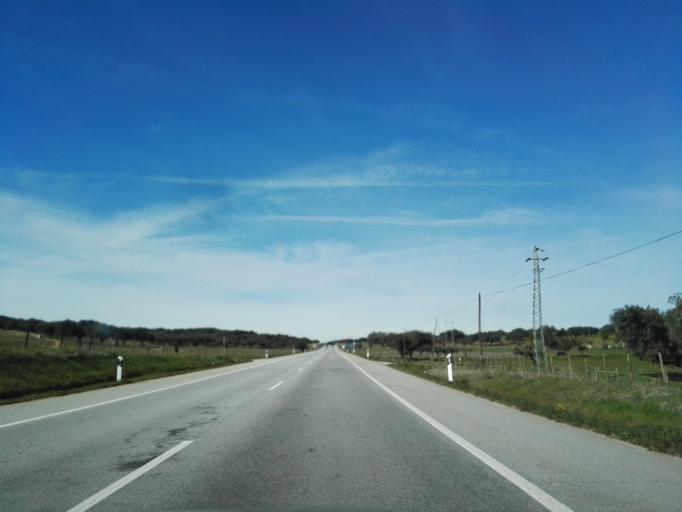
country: PT
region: Portalegre
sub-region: Arronches
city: Arronches
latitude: 39.1679
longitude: -7.3294
